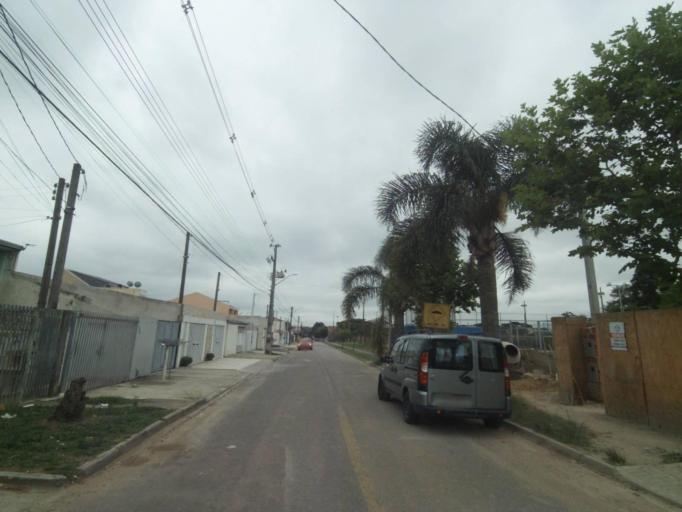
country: BR
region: Parana
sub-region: Araucaria
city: Araucaria
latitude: -25.5496
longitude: -49.3382
